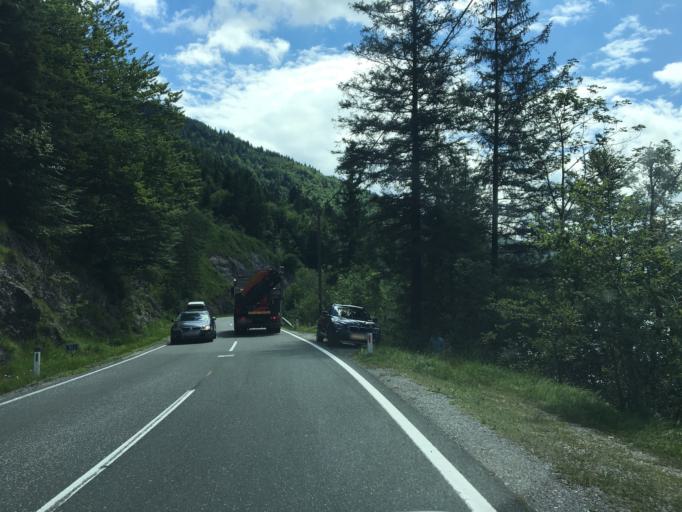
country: AT
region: Salzburg
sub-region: Politischer Bezirk Hallein
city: Krispl
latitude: 47.7472
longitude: 13.1729
